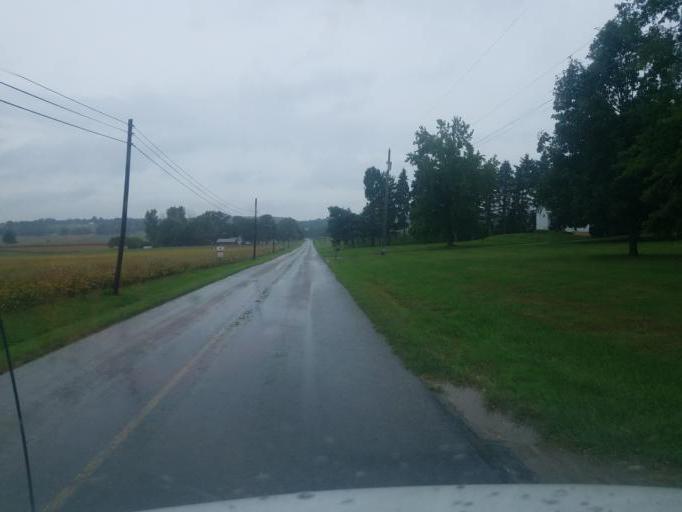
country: US
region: Ohio
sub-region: Wayne County
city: Rittman
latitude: 40.9839
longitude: -81.8046
